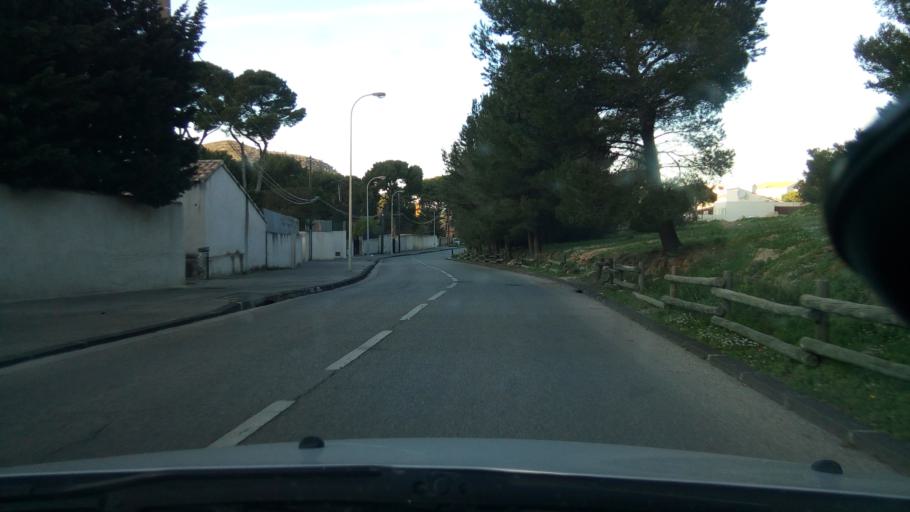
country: FR
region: Provence-Alpes-Cote d'Azur
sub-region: Departement des Bouches-du-Rhone
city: Marseille 09
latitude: 43.2267
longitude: 5.4035
